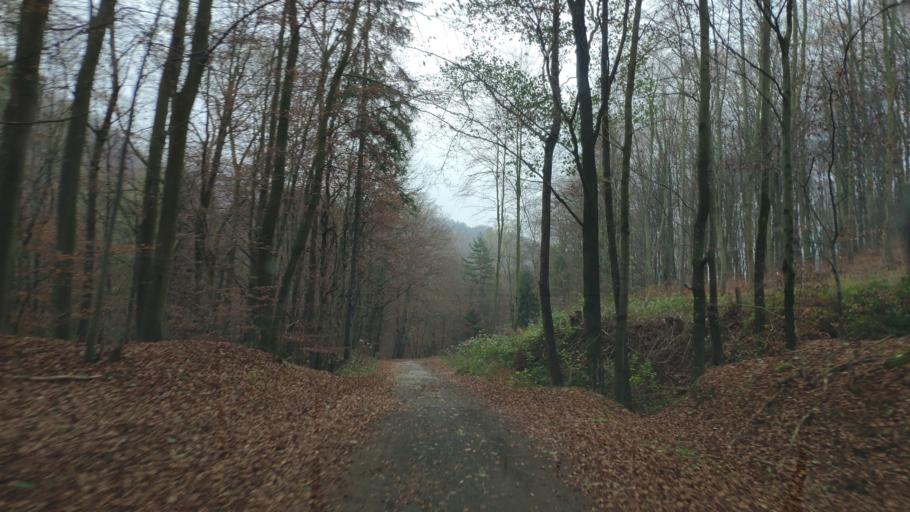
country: SK
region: Presovsky
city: Sabinov
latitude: 49.1487
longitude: 21.2102
